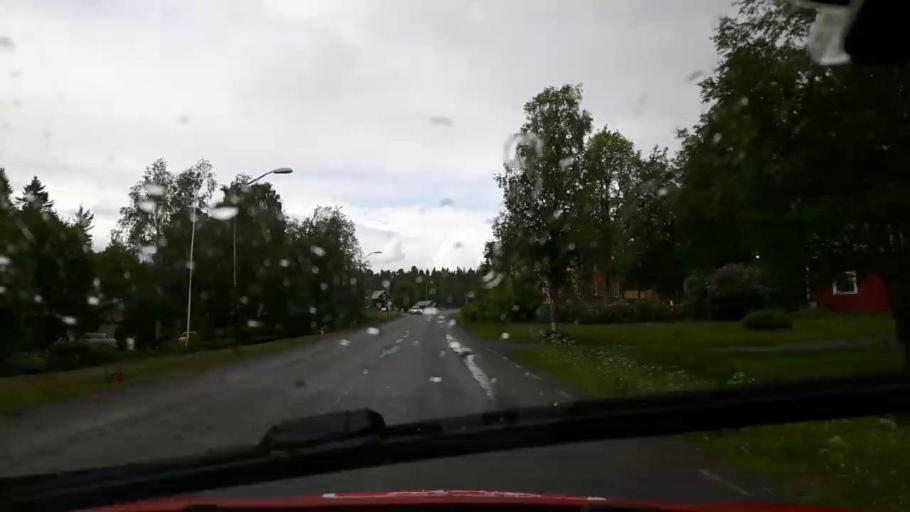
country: SE
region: Jaemtland
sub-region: Krokoms Kommun
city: Krokom
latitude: 63.4554
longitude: 14.1904
